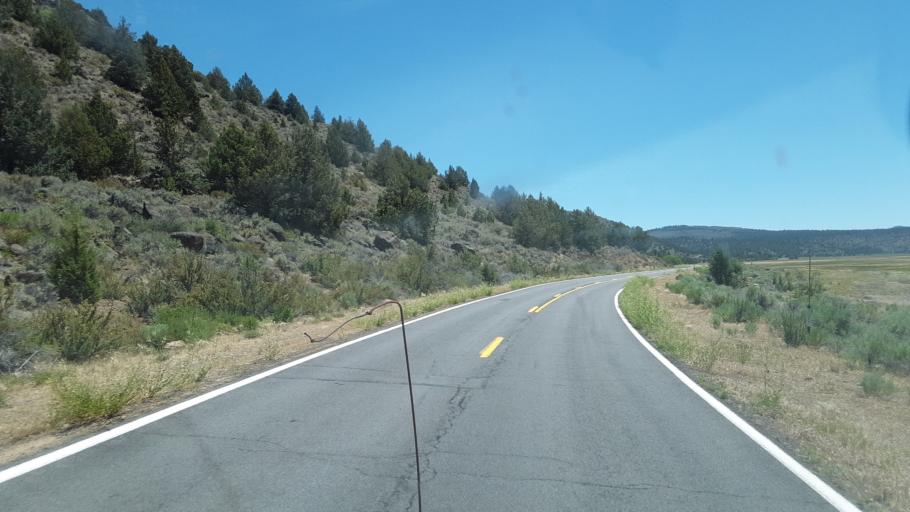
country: US
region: California
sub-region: Lassen County
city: Susanville
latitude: 40.6778
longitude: -120.6596
